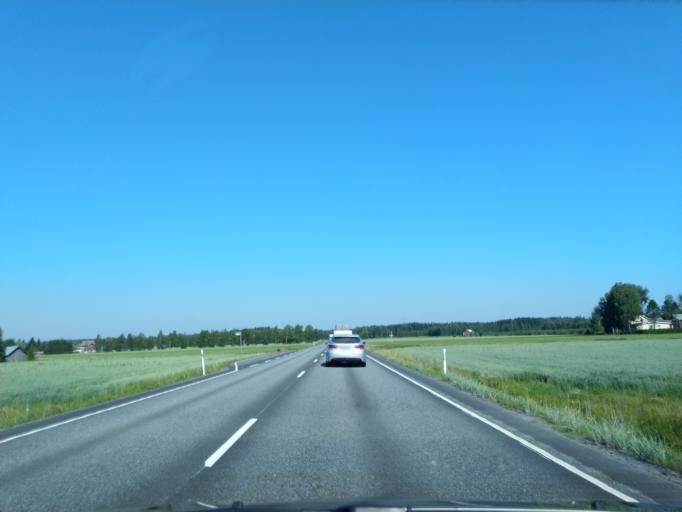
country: FI
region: Varsinais-Suomi
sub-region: Loimaa
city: Alastaro
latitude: 61.0926
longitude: 22.8779
